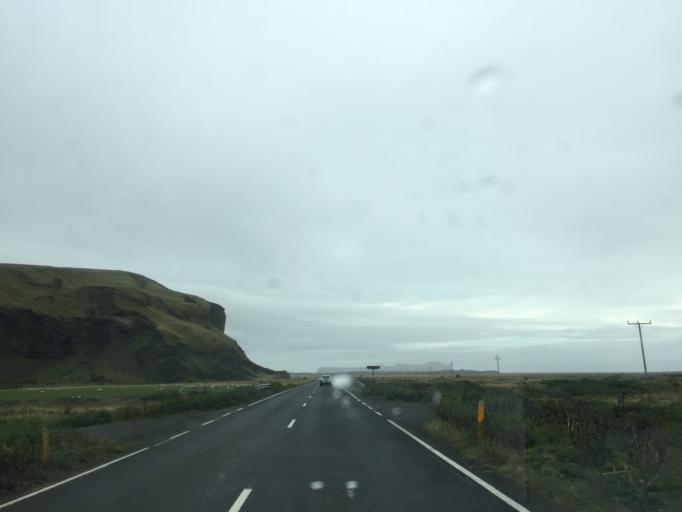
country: IS
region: South
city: Vestmannaeyjar
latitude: 63.4193
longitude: -18.9486
